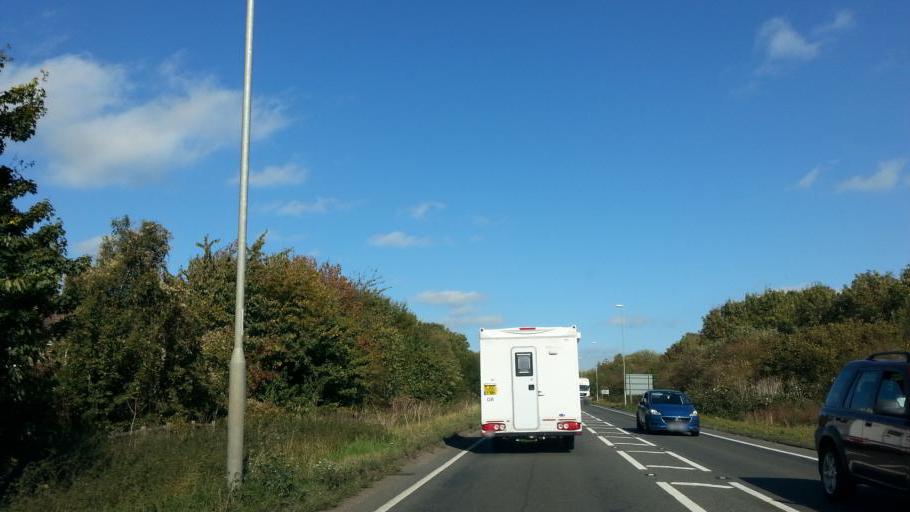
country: GB
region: England
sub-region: Northamptonshire
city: Thrapston
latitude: 52.3952
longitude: -0.5228
